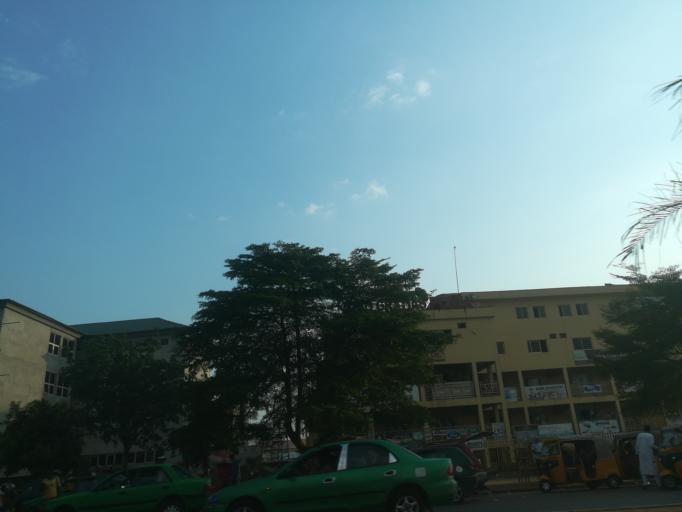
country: NG
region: Abuja Federal Capital Territory
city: Abuja
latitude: 9.0680
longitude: 7.4452
